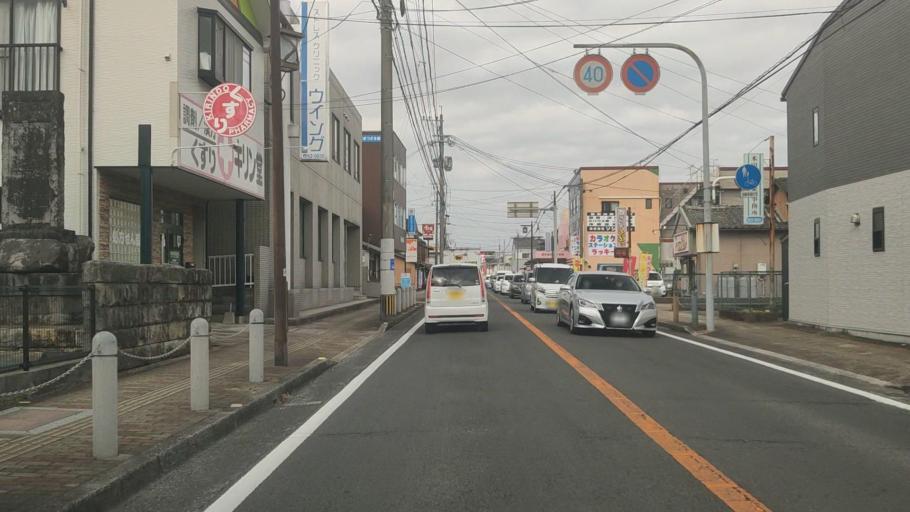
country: JP
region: Nagasaki
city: Shimabara
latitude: 32.7908
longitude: 130.3699
